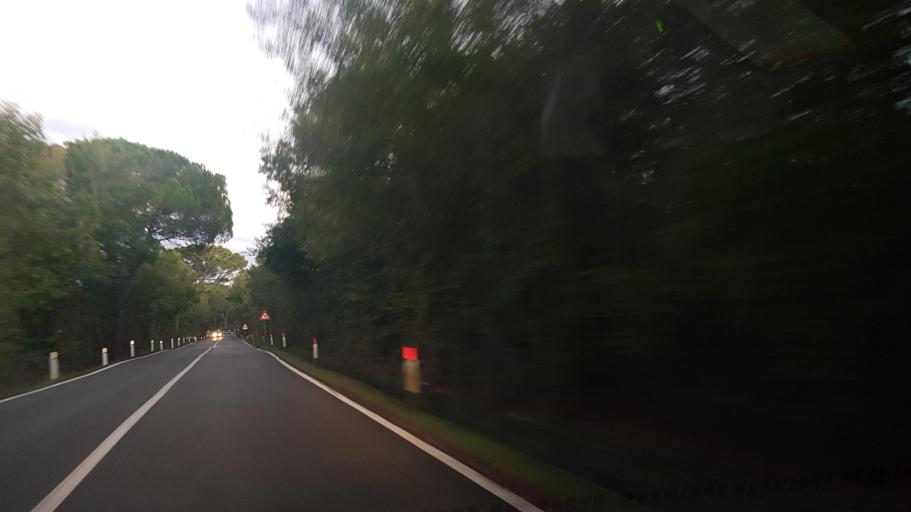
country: IT
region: Basilicate
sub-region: Provincia di Matera
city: Matera
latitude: 40.6770
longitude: 16.6611
